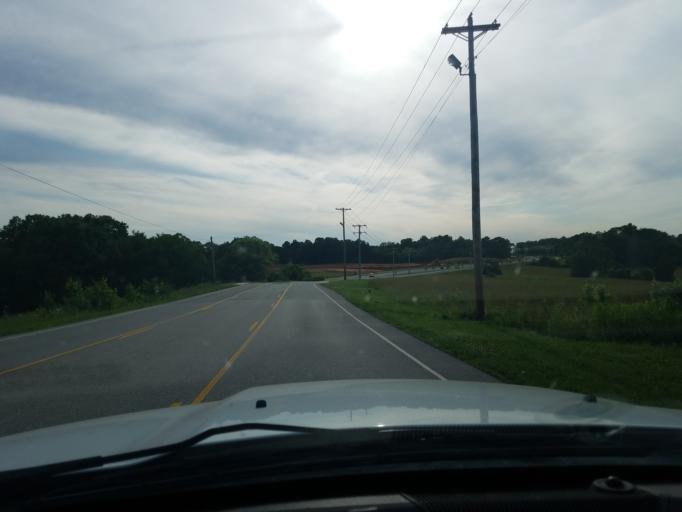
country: US
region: Tennessee
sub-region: Putnam County
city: Cookeville
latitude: 36.1293
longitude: -85.5480
